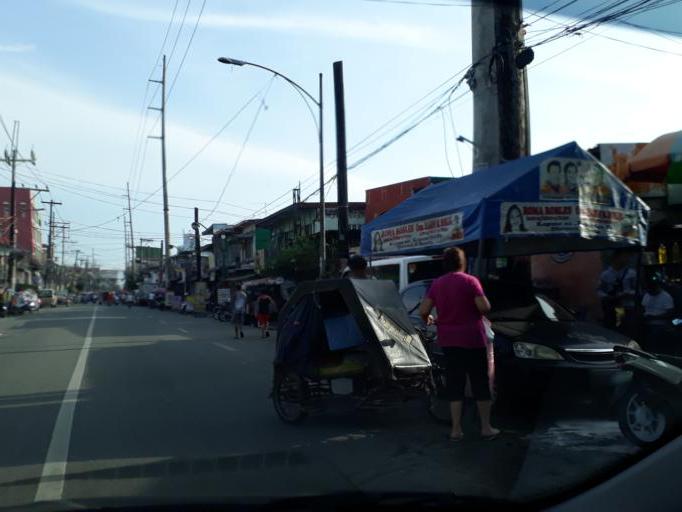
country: PH
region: Metro Manila
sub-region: City of Manila
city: Manila
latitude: 14.6322
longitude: 120.9746
